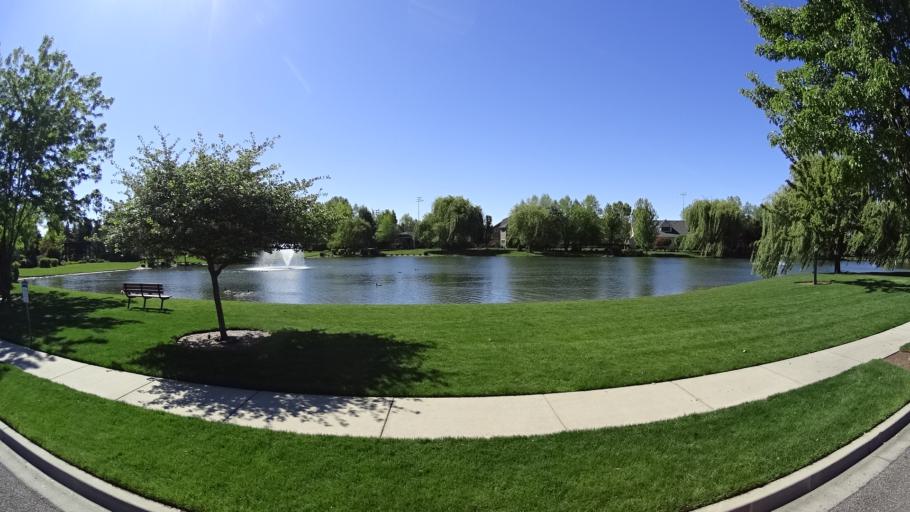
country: US
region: Idaho
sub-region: Ada County
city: Meridian
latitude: 43.6573
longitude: -116.4085
